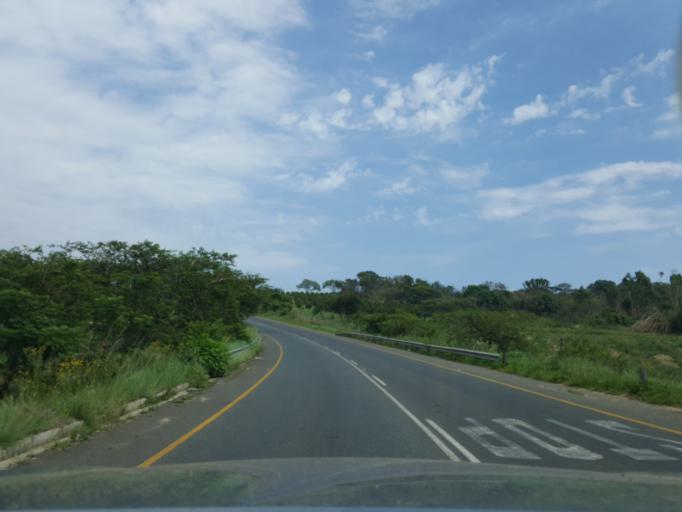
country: ZA
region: Mpumalanga
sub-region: Ehlanzeni District
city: White River
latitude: -25.3749
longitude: 31.0809
